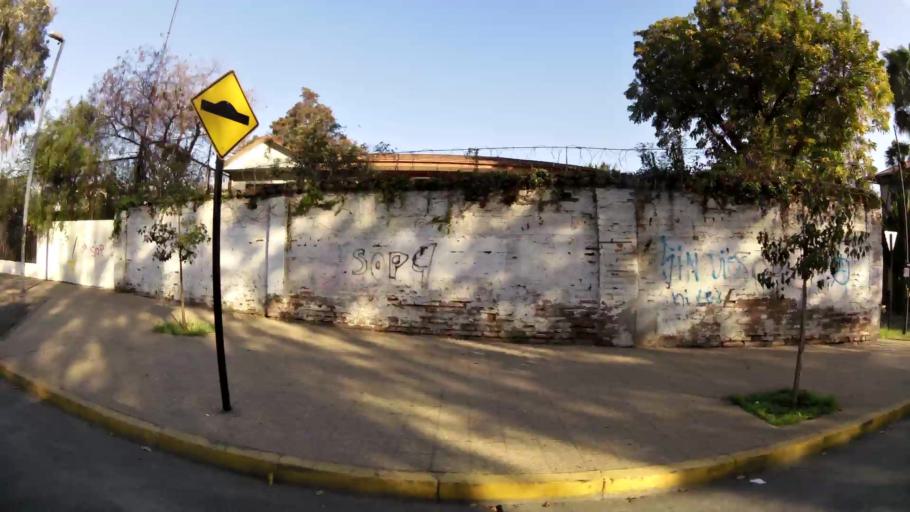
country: CL
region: Santiago Metropolitan
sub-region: Provincia de Santiago
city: Santiago
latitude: -33.4301
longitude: -70.6299
